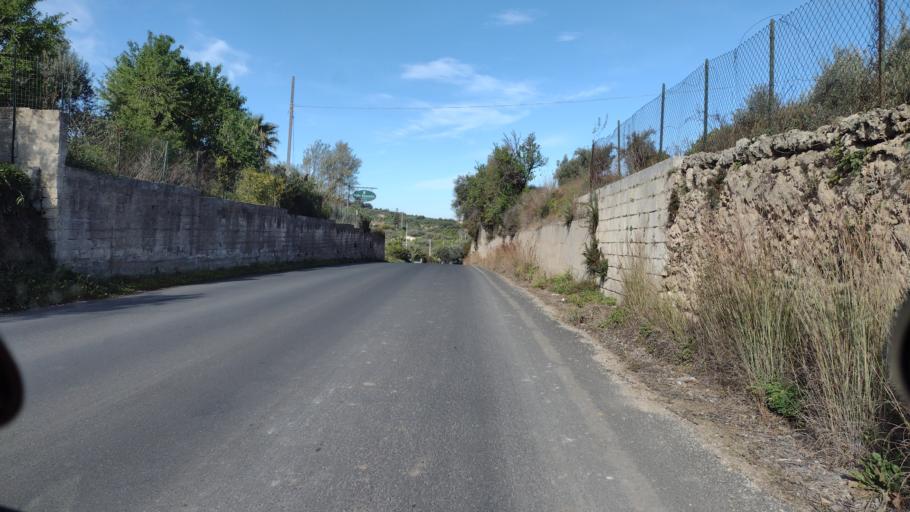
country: IT
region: Sicily
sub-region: Provincia di Siracusa
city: Noto
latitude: 36.8765
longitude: 15.1001
